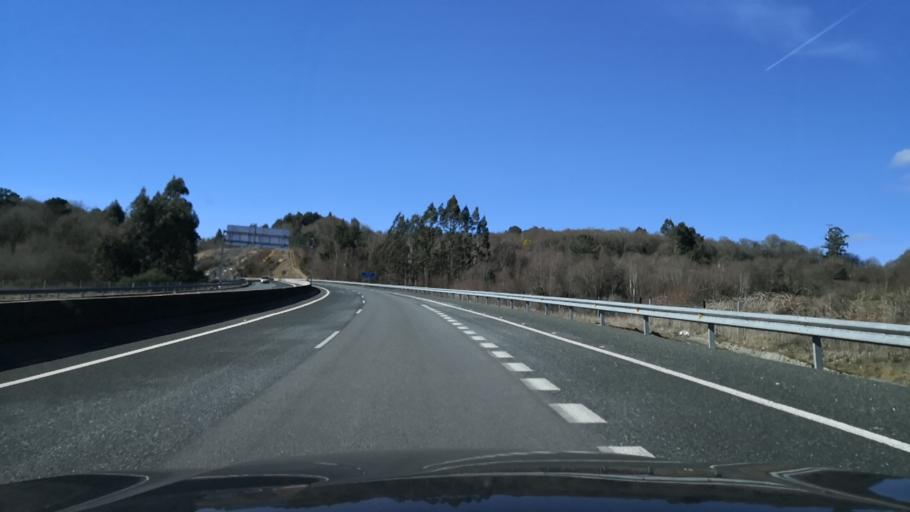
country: ES
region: Galicia
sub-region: Provincia de Pontevedra
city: Lalin
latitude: 42.6233
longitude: -8.1017
